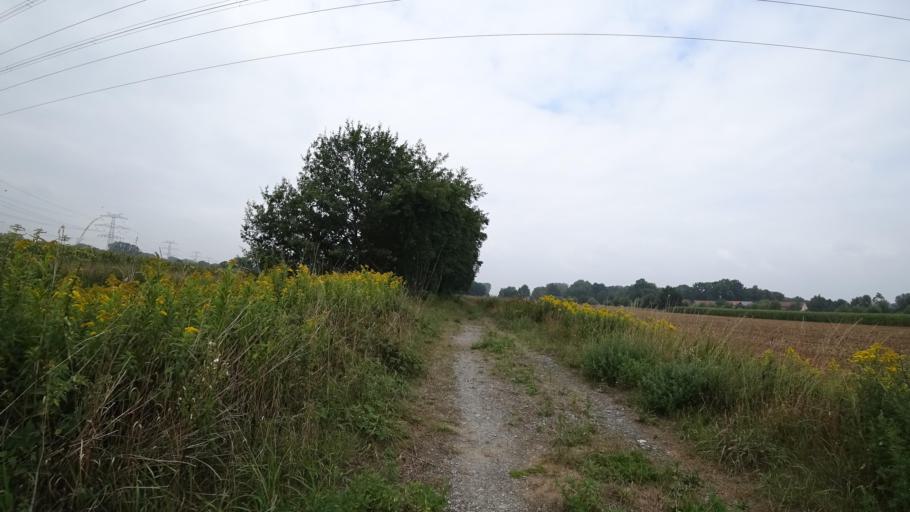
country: DE
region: North Rhine-Westphalia
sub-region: Regierungsbezirk Detmold
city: Guetersloh
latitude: 51.9045
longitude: 8.3242
